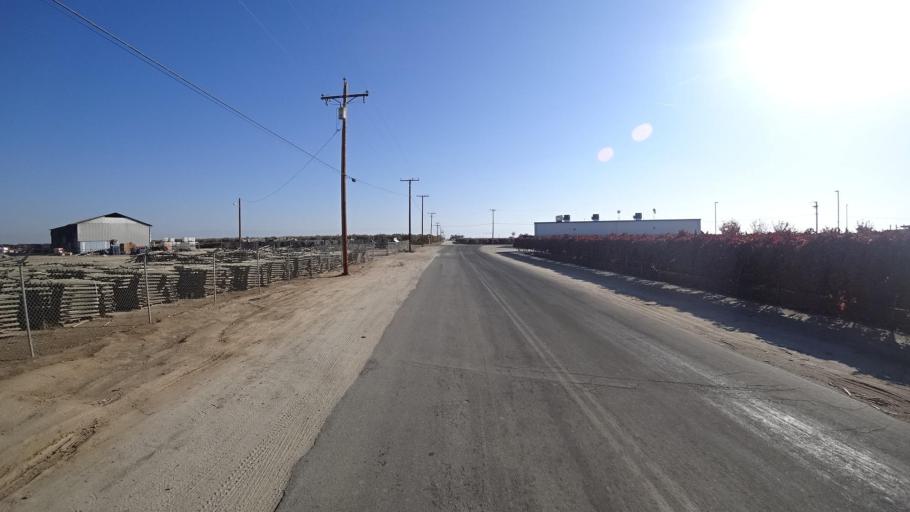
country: US
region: California
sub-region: Tulare County
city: Richgrove
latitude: 35.7471
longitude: -119.1427
